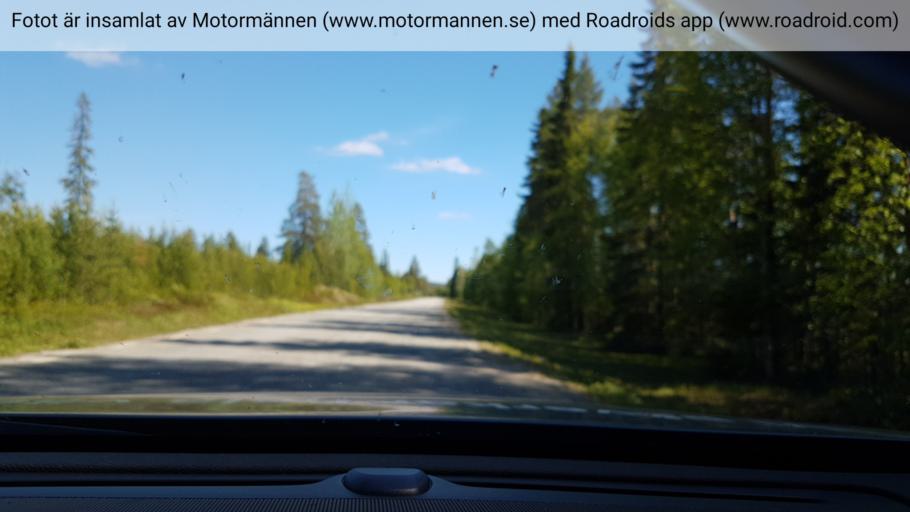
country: SE
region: Vaesterbotten
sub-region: Lycksele Kommun
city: Soderfors
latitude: 64.6305
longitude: 18.0361
